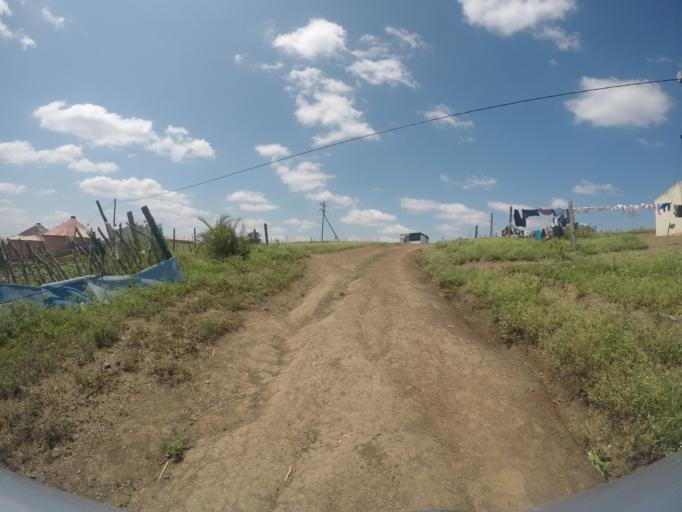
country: ZA
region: KwaZulu-Natal
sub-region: uThungulu District Municipality
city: Empangeni
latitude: -28.6105
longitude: 31.7341
